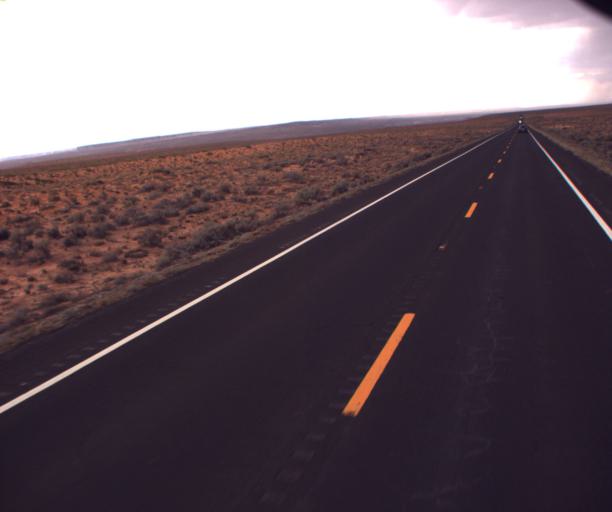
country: US
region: Arizona
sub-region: Coconino County
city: Tuba City
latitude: 36.2044
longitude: -111.0553
